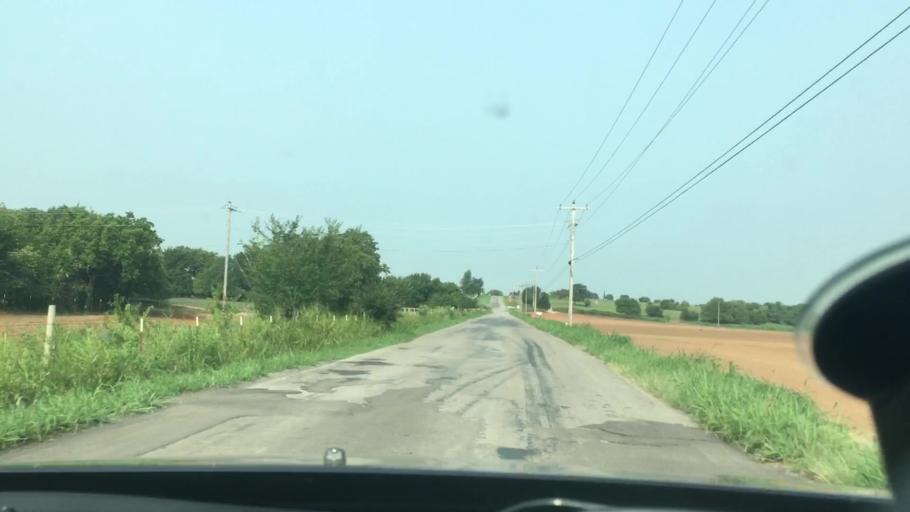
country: US
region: Oklahoma
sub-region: Garvin County
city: Lindsay
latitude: 34.8121
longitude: -97.6288
